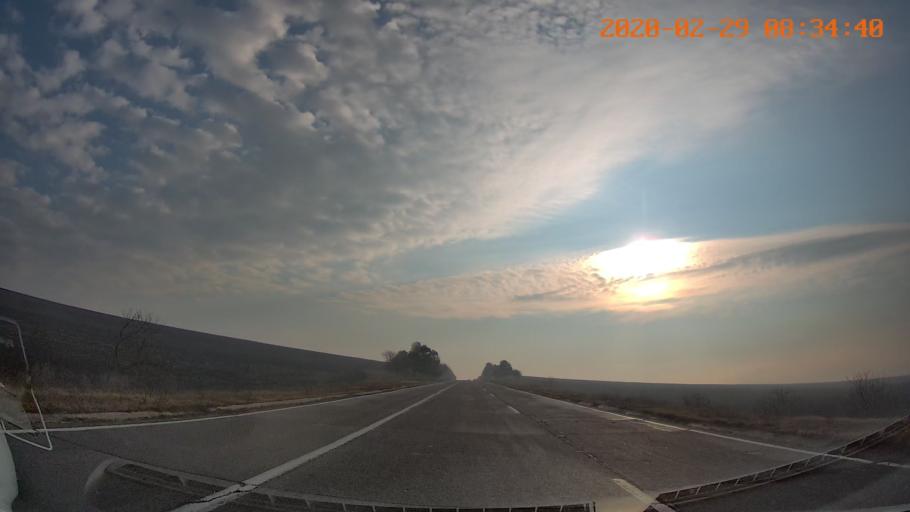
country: MD
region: Anenii Noi
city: Anenii Noi
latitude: 46.9243
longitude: 29.3134
